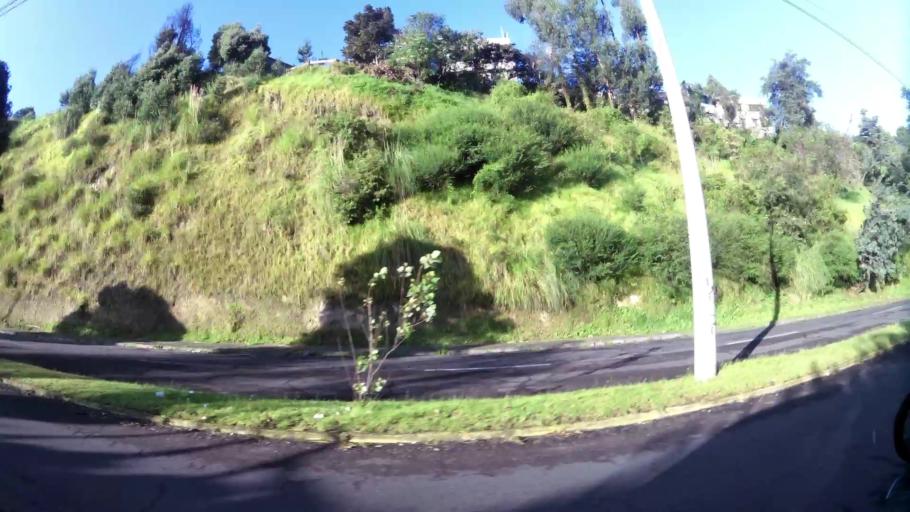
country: EC
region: Pichincha
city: Quito
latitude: -0.2343
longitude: -78.5107
